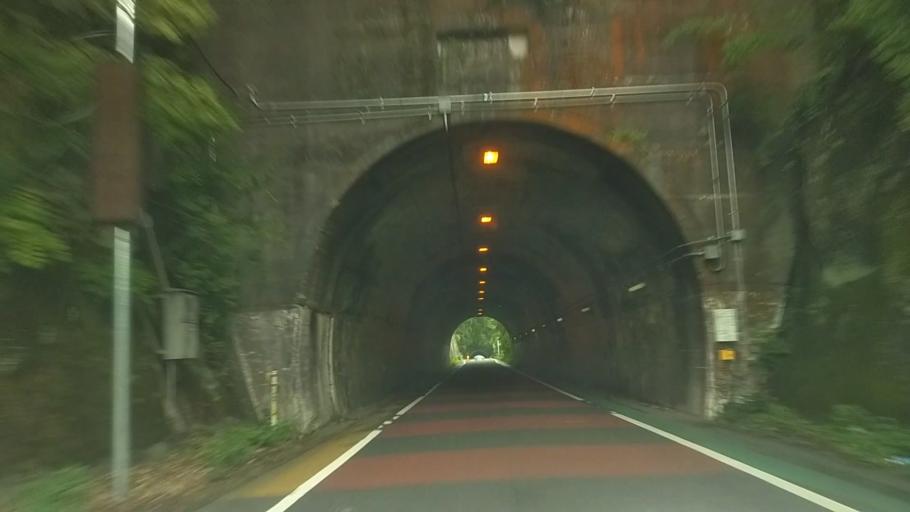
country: JP
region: Chiba
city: Kawaguchi
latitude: 35.2528
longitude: 140.0692
